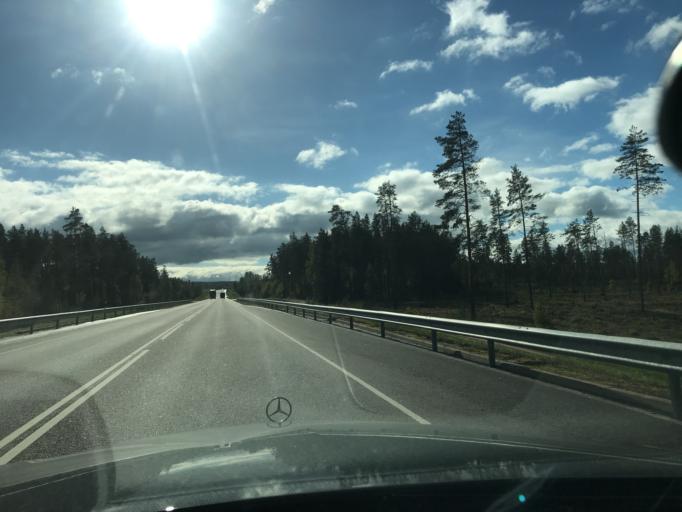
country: EE
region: Vorumaa
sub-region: Voru linn
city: Voru
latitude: 57.8248
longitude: 27.0636
